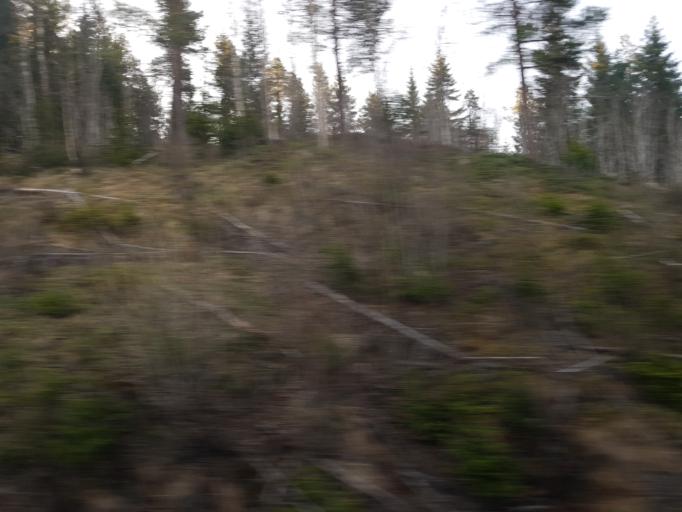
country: NO
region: Sor-Trondelag
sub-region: Rennebu
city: Berkak
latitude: 62.8711
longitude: 10.0872
